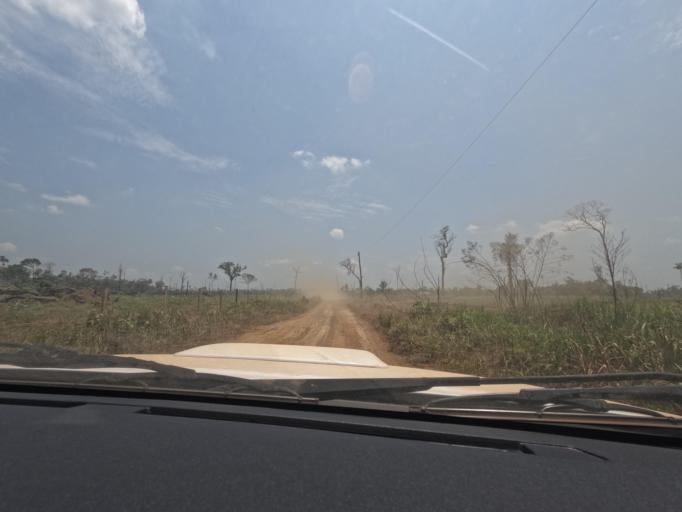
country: BR
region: Rondonia
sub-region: Porto Velho
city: Porto Velho
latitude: -8.6466
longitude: -64.1746
